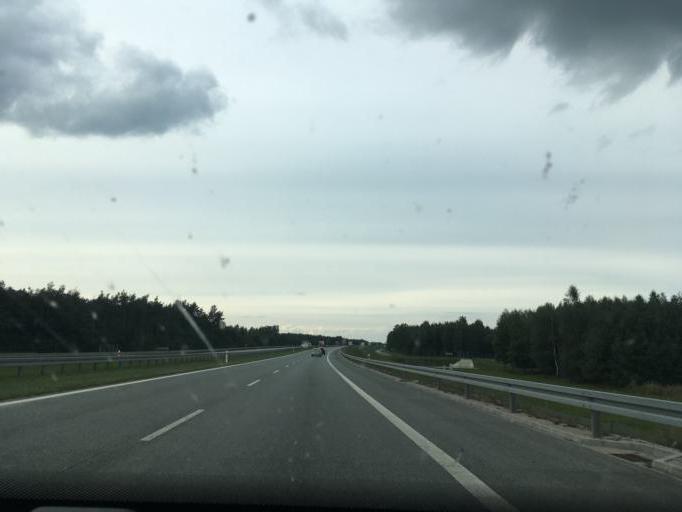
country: PL
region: Lodz Voivodeship
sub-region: Powiat zdunskowolski
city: Zdunska Wola
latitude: 51.5816
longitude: 18.9065
